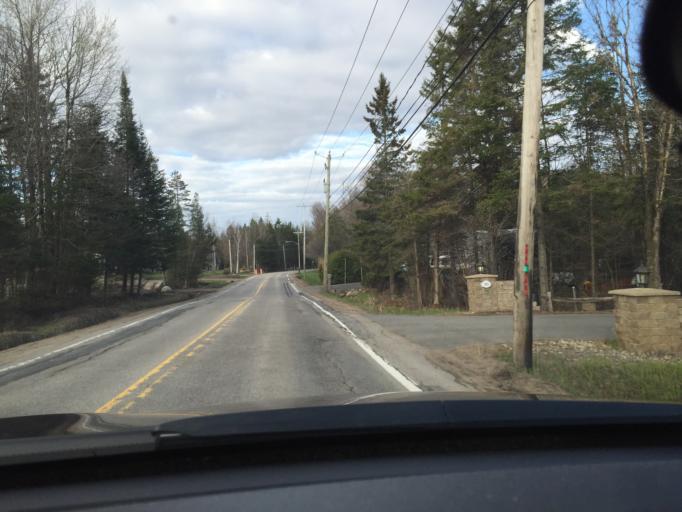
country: CA
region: Quebec
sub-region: Capitale-Nationale
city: Sainte Catherine de la Jacques Cartier
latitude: 46.8491
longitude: -71.5784
